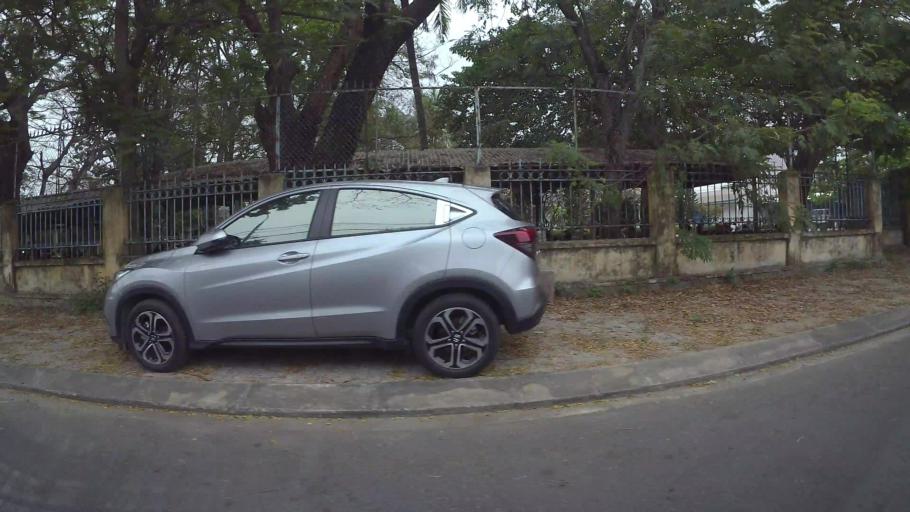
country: VN
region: Da Nang
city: Cam Le
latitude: 16.0294
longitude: 108.2093
